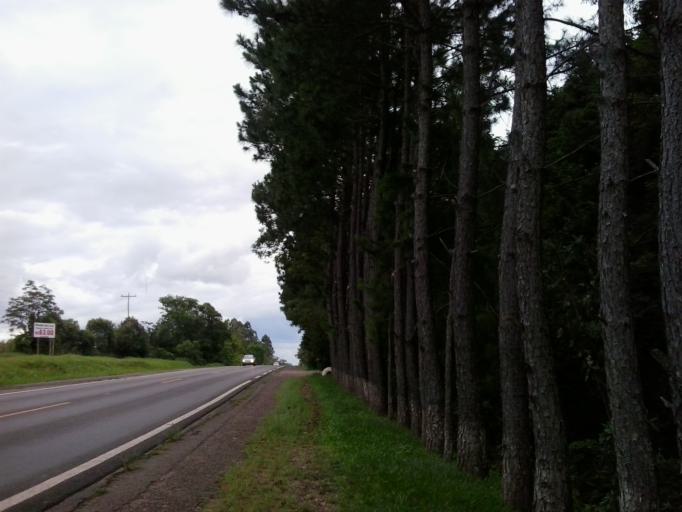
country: BR
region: Rio Grande do Sul
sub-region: Santa Maria
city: Santa Maria
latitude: -29.7320
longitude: -53.5449
